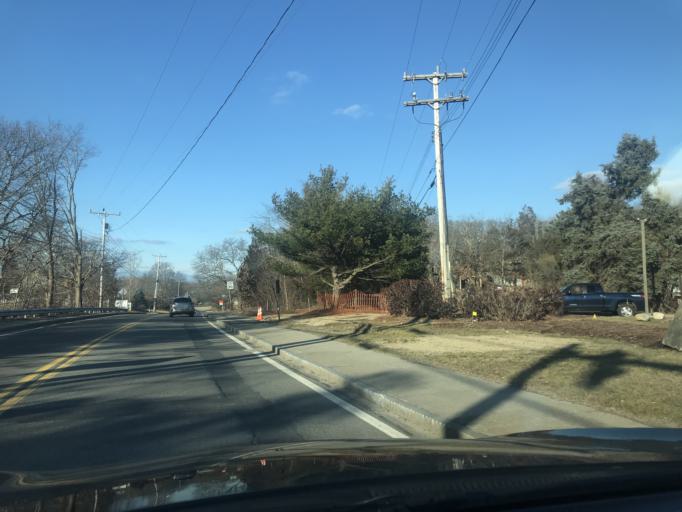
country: US
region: Massachusetts
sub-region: Plymouth County
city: Plymouth
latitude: 41.9389
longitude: -70.6570
